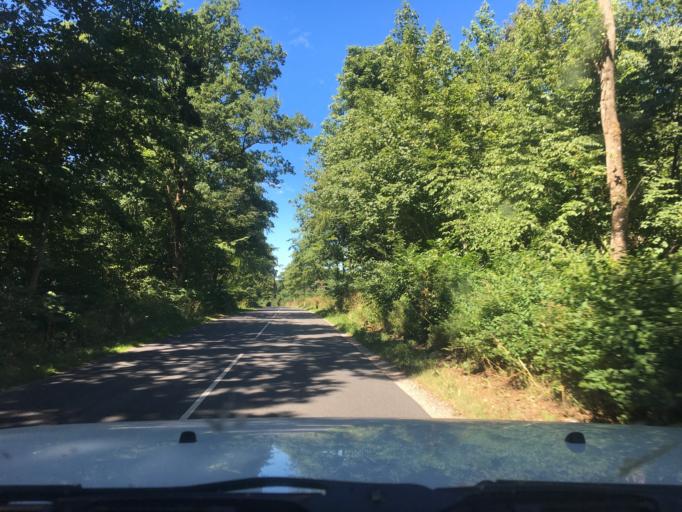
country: DK
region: Central Jutland
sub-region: Syddjurs Kommune
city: Hornslet
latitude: 56.3320
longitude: 10.3375
